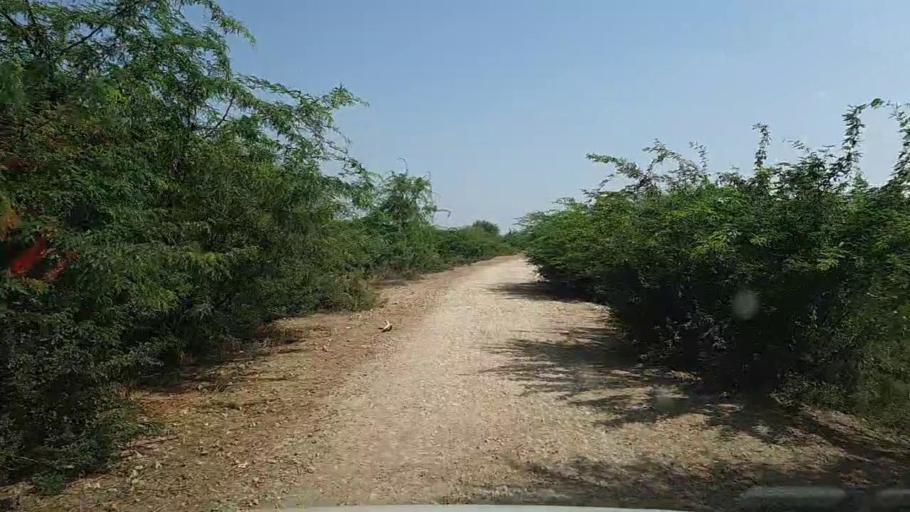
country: PK
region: Sindh
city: Kario
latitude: 24.8366
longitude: 68.7089
